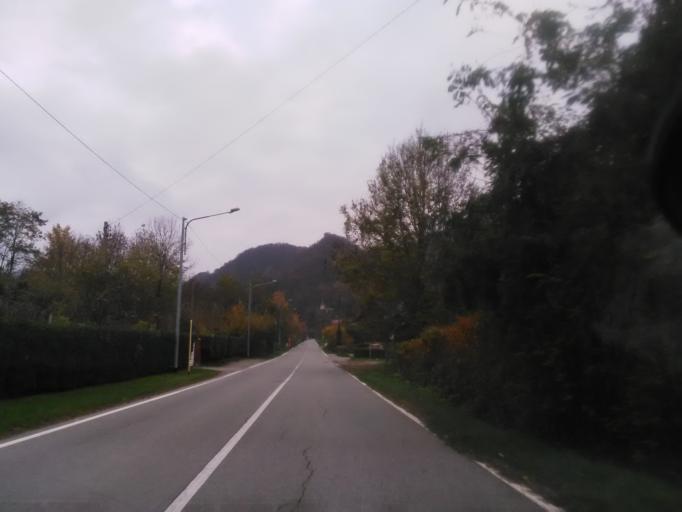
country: IT
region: Piedmont
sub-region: Provincia di Vercelli
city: Varallo
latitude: 45.8094
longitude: 8.2585
